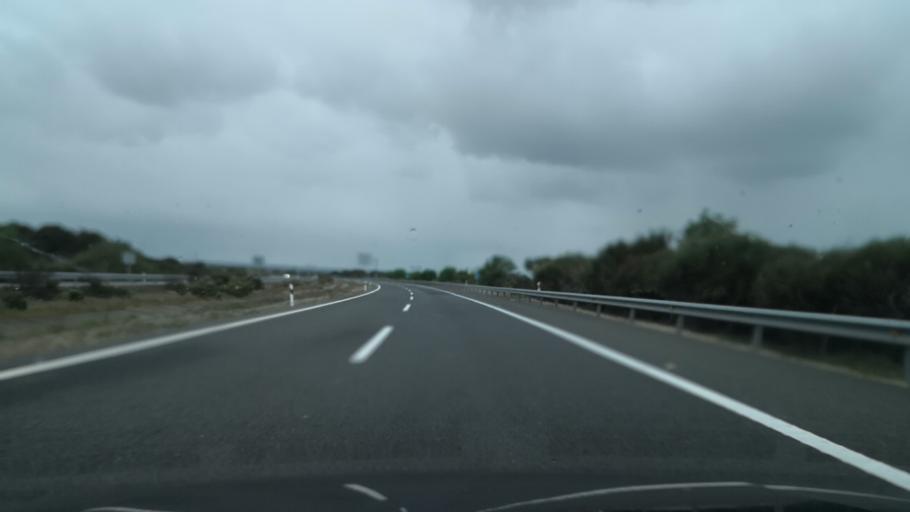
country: ES
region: Extremadura
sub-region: Provincia de Caceres
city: Abadia
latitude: 40.2402
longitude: -5.9668
